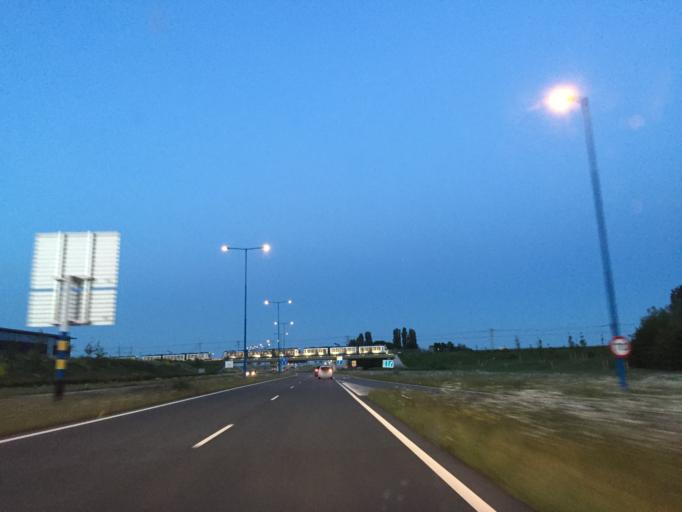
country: NL
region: South Holland
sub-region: Gemeente Rijnwoude
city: Benthuizen
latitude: 52.0504
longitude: 4.5297
